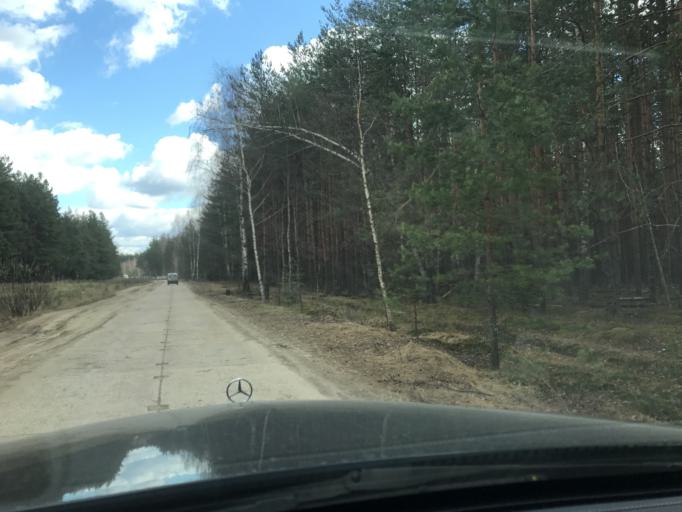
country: RU
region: Vladimir
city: Pokrov
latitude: 55.8643
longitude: 39.2203
